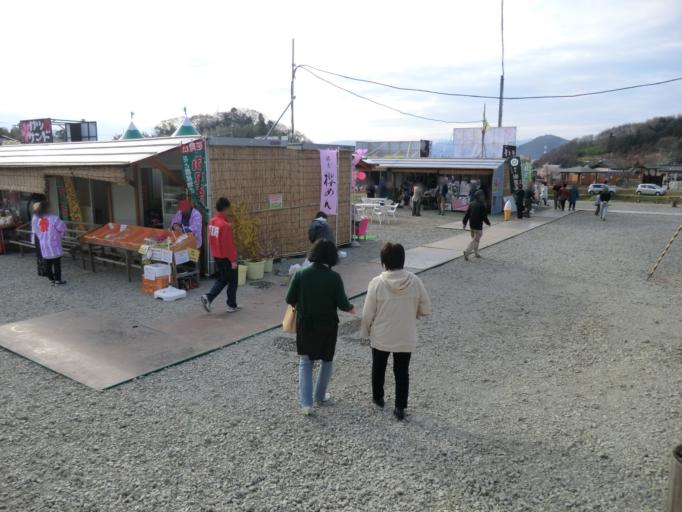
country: JP
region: Fukushima
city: Fukushima-shi
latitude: 37.7447
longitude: 140.4915
